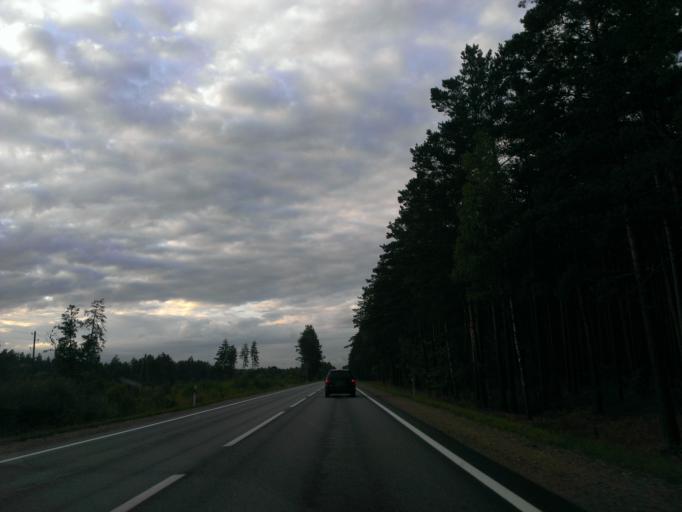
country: LV
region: Salaspils
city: Salaspils
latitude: 56.9333
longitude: 24.3873
